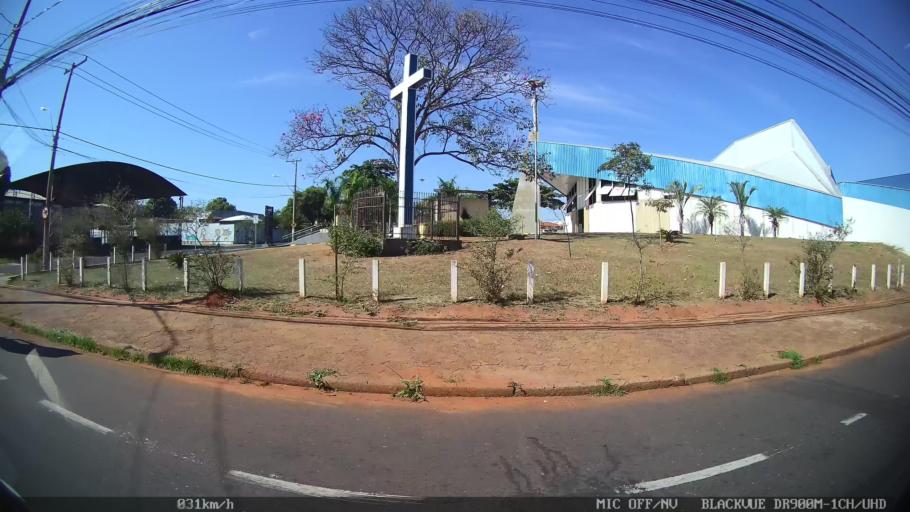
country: BR
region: Sao Paulo
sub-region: Sao Jose Do Rio Preto
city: Sao Jose do Rio Preto
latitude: -20.8060
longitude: -49.4021
